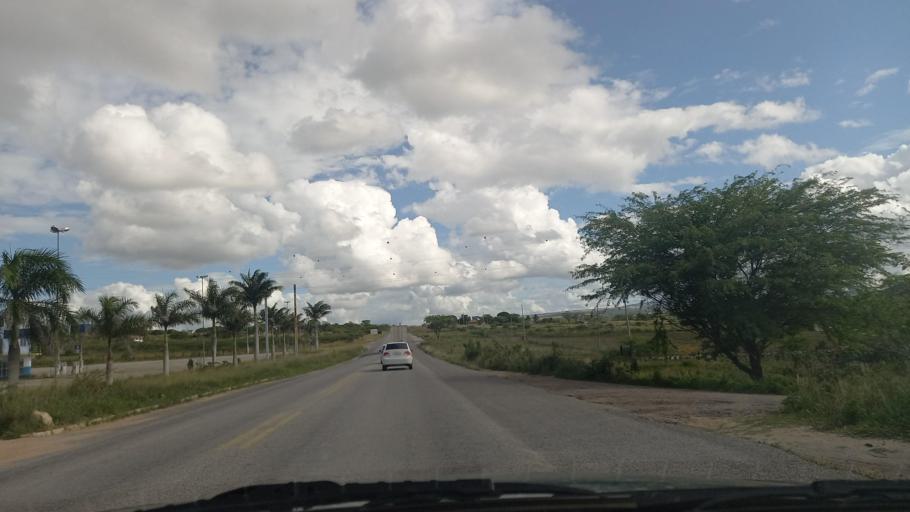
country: BR
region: Pernambuco
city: Garanhuns
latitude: -8.8051
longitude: -36.4412
